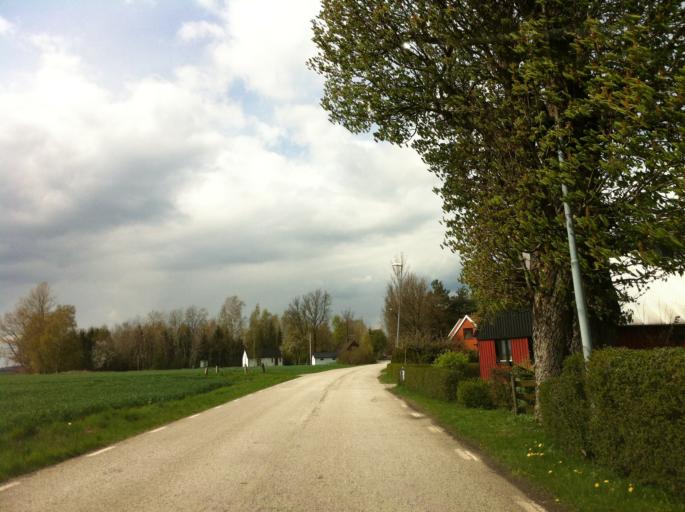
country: SE
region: Skane
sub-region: Kavlinge Kommun
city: Kaevlinge
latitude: 55.8094
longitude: 13.1469
